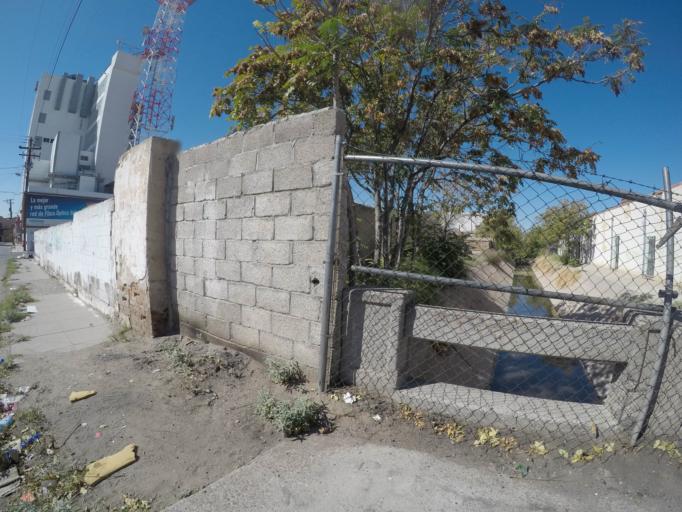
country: MX
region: Chihuahua
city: Ciudad Juarez
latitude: 31.7402
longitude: -106.4795
